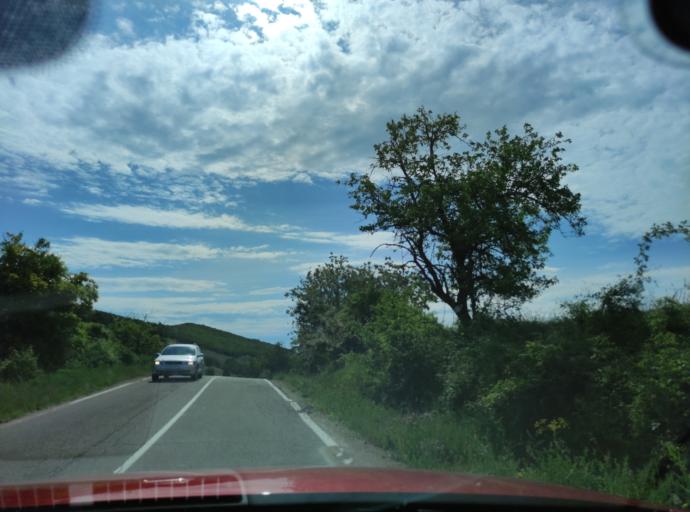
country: BG
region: Montana
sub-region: Obshtina Chiprovtsi
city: Chiprovtsi
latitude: 43.4771
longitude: 22.8389
